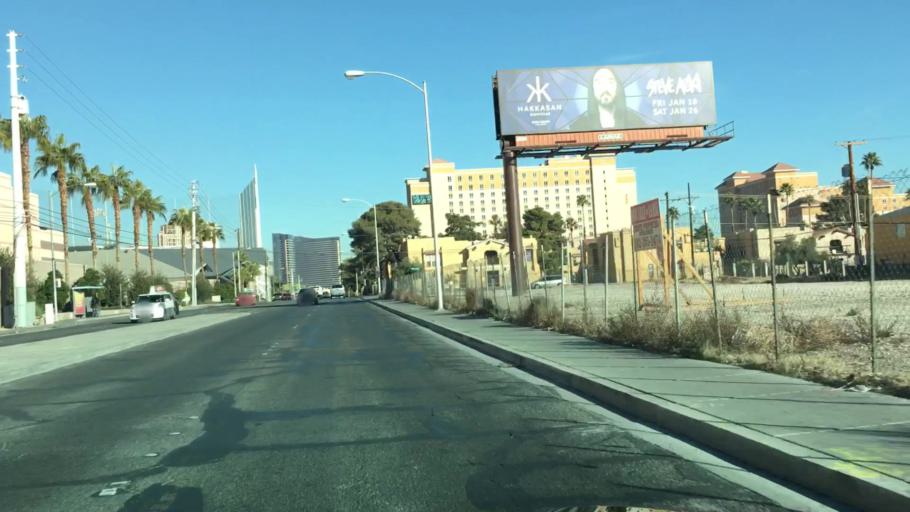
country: US
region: Nevada
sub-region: Clark County
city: Paradise
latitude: 36.1035
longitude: -115.1638
